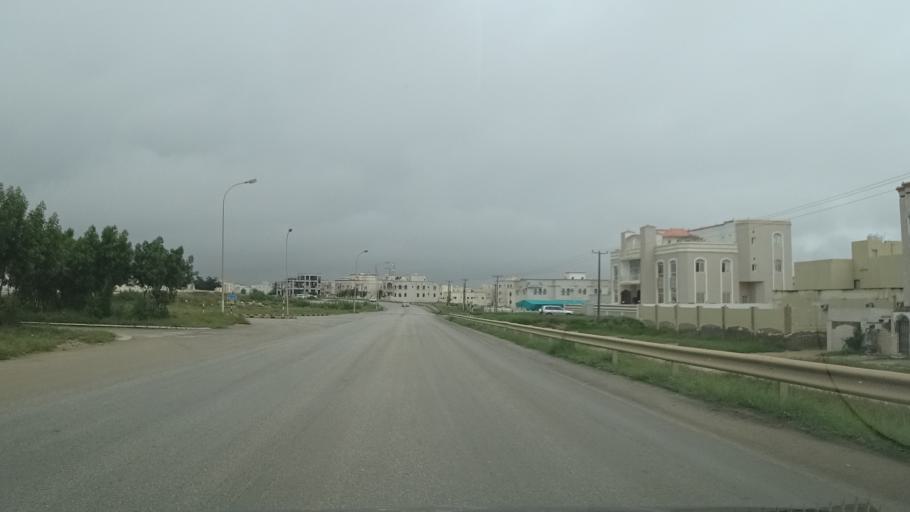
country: OM
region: Zufar
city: Salalah
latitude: 17.0060
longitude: 54.0325
